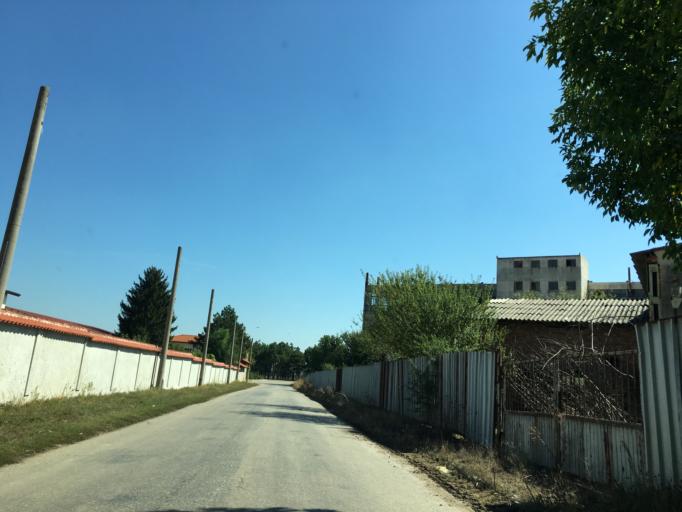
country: BG
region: Pleven
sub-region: Obshtina Knezha
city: Knezha
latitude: 43.5141
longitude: 24.0936
